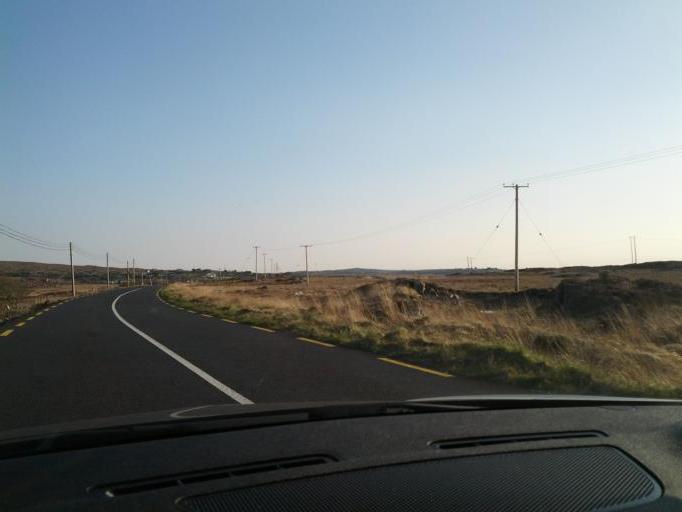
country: IE
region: Connaught
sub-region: County Galway
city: Oughterard
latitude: 53.3314
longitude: -9.5449
